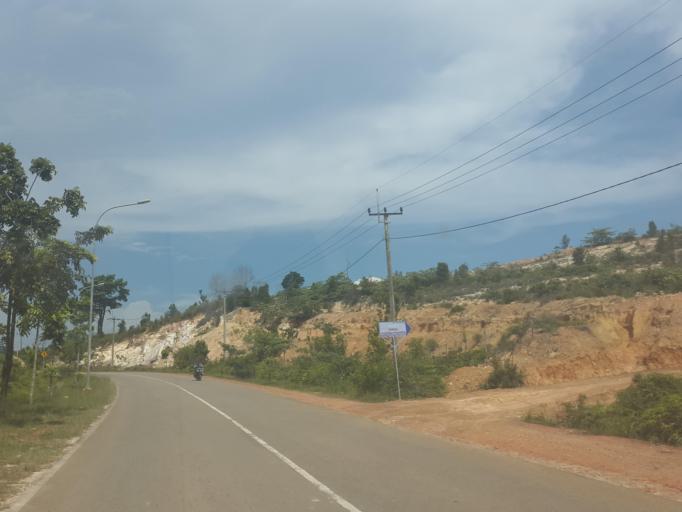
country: ID
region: Riau Islands
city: Tanjungpinang
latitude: 0.9463
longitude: 104.0573
